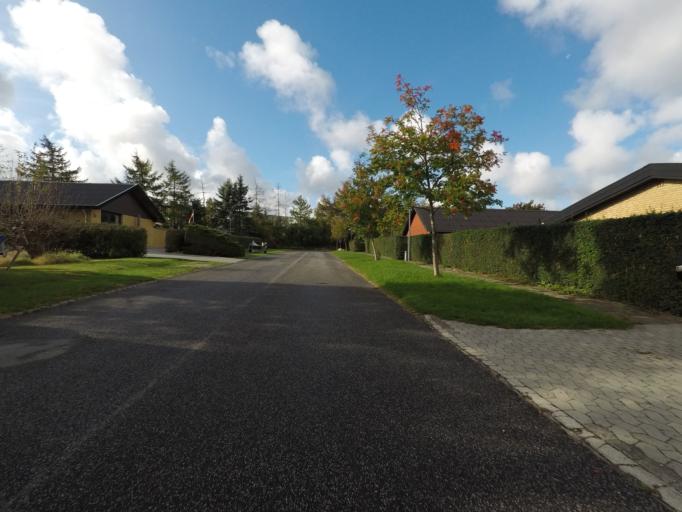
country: DK
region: Capital Region
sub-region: Egedal Kommune
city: Smorumnedre
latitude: 55.7324
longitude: 12.2997
